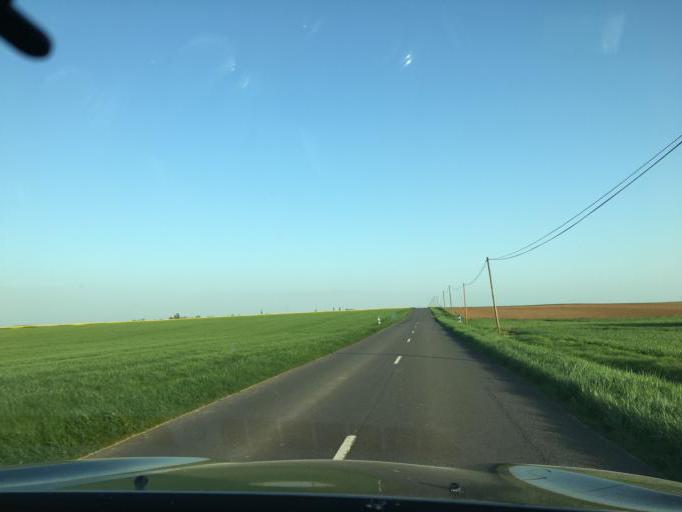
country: FR
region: Centre
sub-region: Departement du Loir-et-Cher
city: Ouzouer-le-Marche
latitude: 47.8510
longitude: 1.5260
